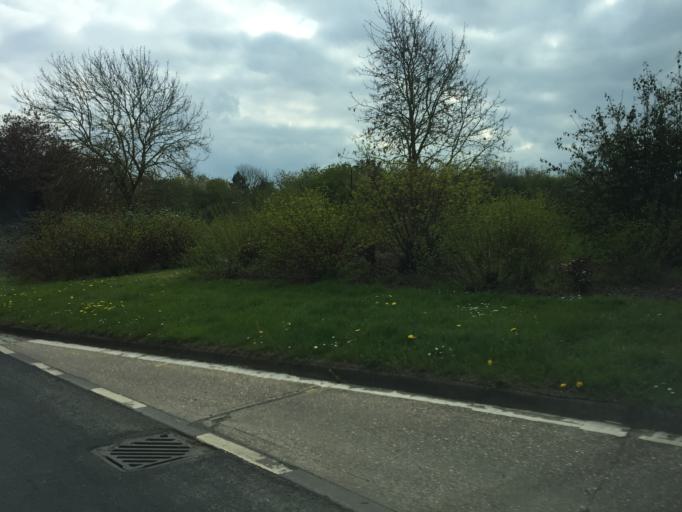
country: GB
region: England
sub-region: Milton Keynes
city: Milton Keynes
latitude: 52.0578
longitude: -0.7552
